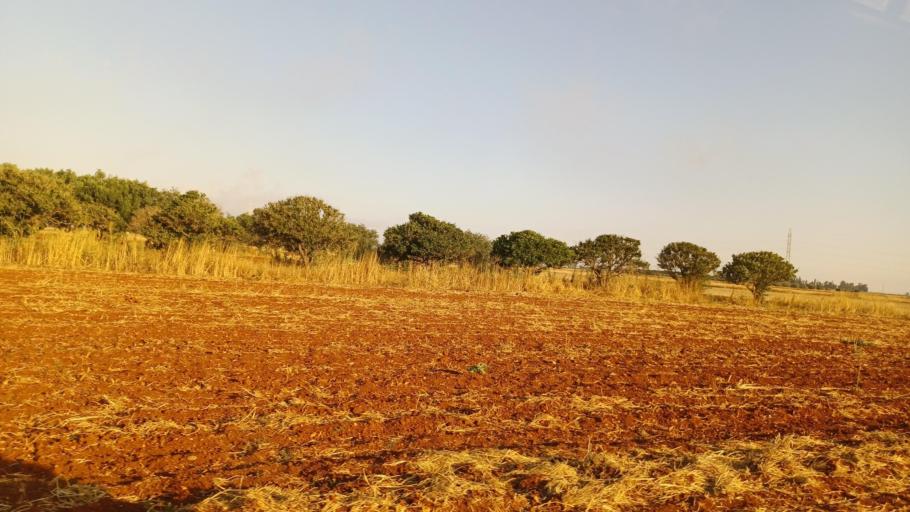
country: CY
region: Ammochostos
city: Avgorou
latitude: 35.0352
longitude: 33.8645
